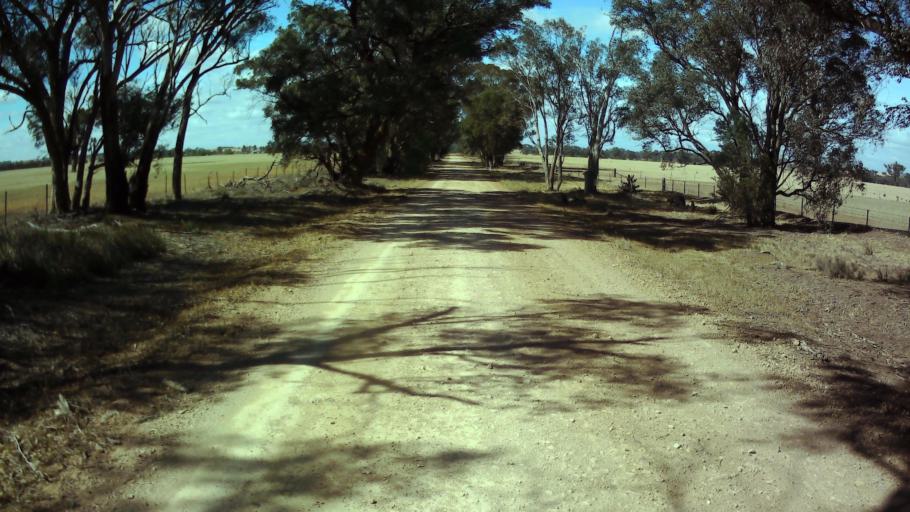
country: AU
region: New South Wales
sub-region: Weddin
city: Grenfell
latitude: -34.0516
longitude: 148.3138
